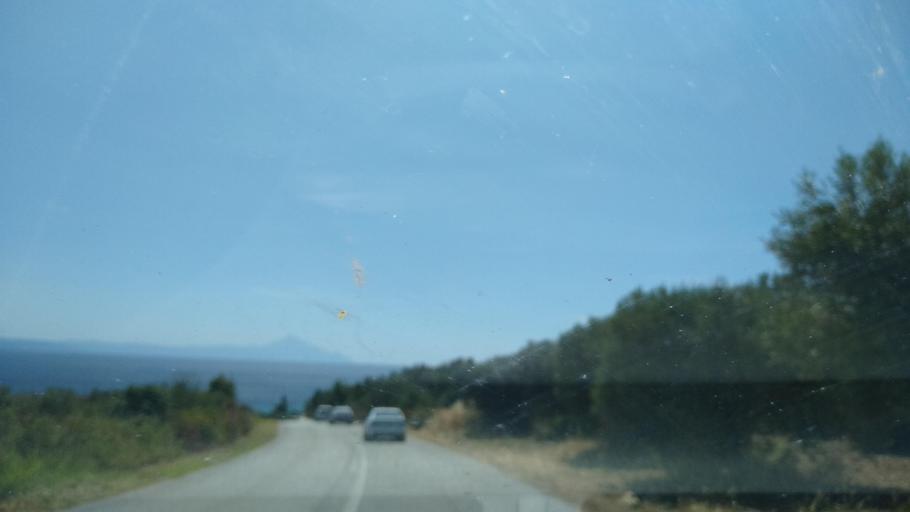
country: GR
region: Central Macedonia
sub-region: Nomos Chalkidikis
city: Agios Nikolaos
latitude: 40.3039
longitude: 23.6886
